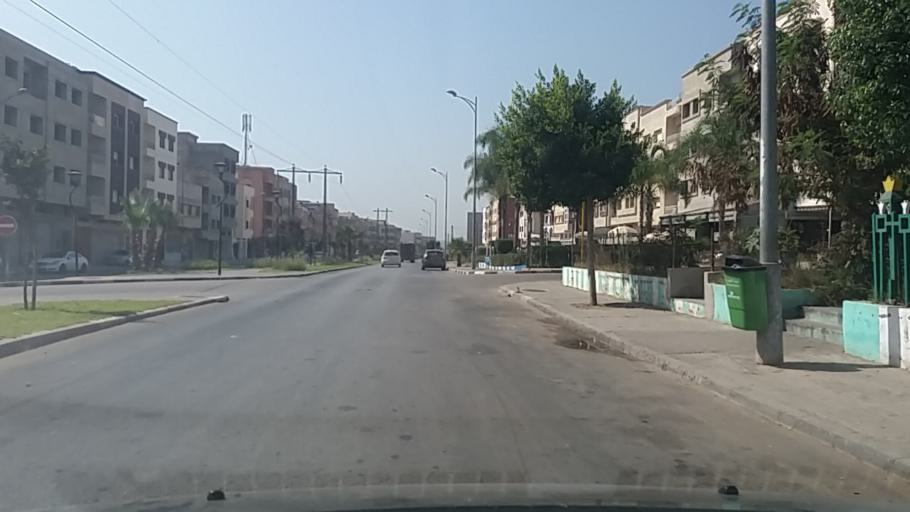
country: MA
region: Gharb-Chrarda-Beni Hssen
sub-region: Kenitra Province
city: Kenitra
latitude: 34.2548
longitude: -6.6153
